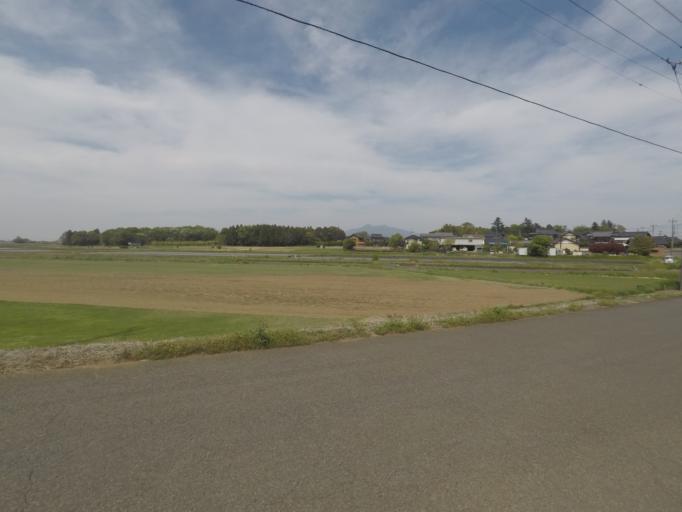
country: JP
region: Ibaraki
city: Ishige
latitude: 36.1222
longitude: 140.0231
